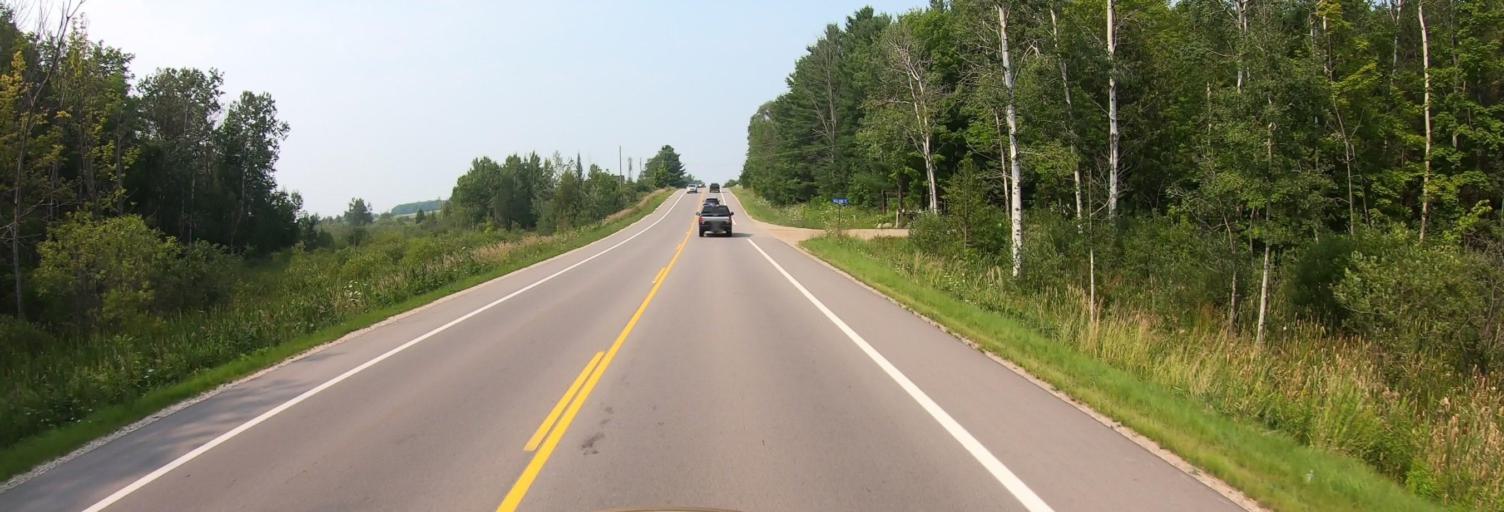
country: US
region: Michigan
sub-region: Charlevoix County
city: Charlevoix
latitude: 45.2278
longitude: -85.2613
